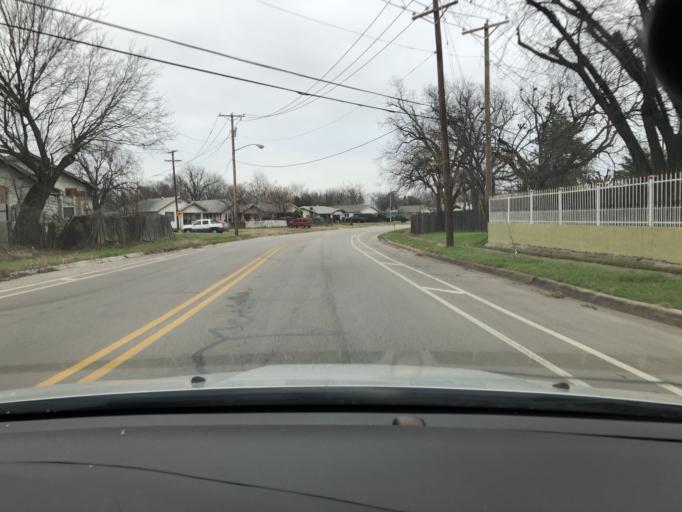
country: US
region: Texas
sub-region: Tarrant County
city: Fort Worth
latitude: 32.7265
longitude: -97.3111
